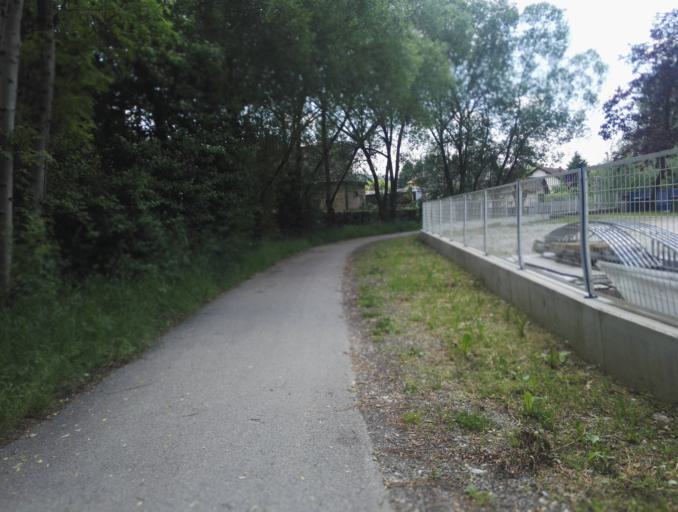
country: AT
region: Styria
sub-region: Politischer Bezirk Graz-Umgebung
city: Stattegg
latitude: 47.1266
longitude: 15.4432
